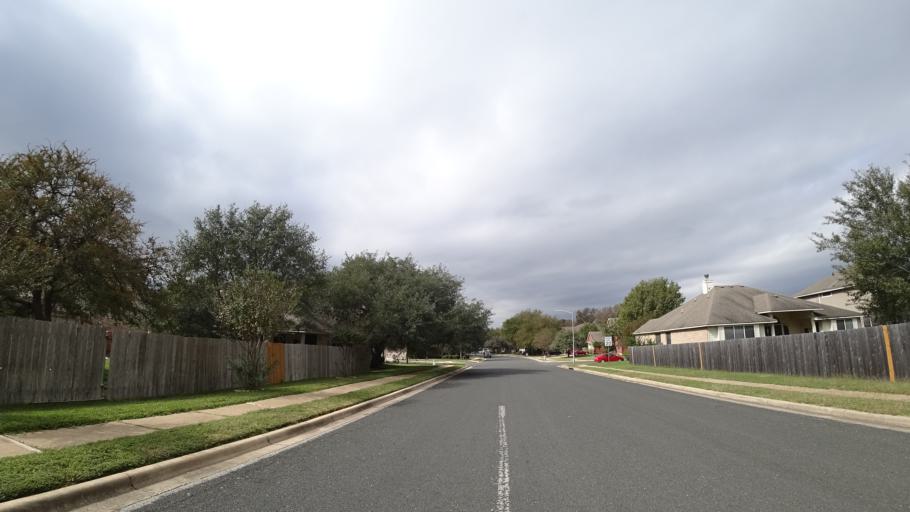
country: US
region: Texas
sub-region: Travis County
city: Shady Hollow
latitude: 30.1563
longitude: -97.8520
